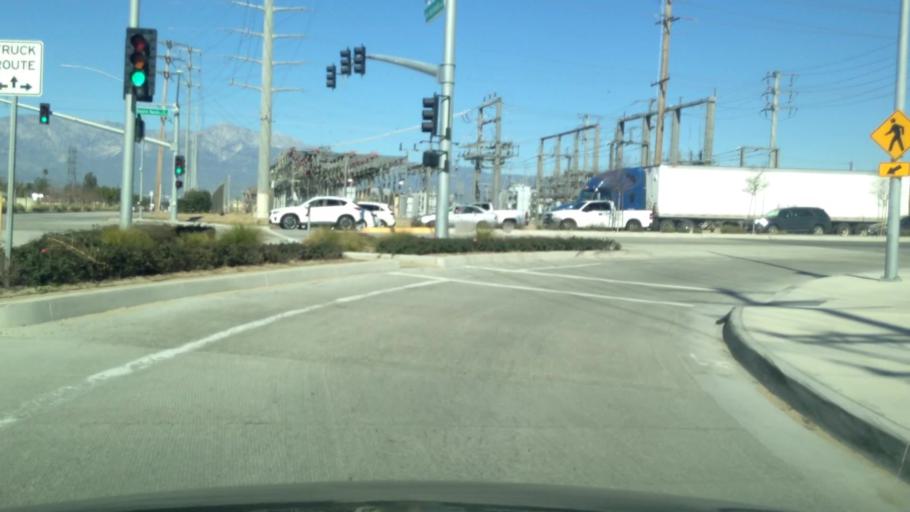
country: US
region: California
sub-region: Riverside County
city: Mira Loma
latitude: 33.9968
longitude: -117.5931
